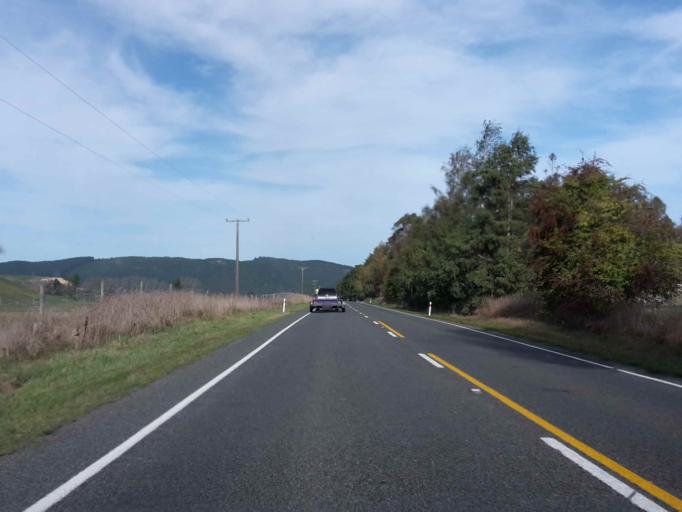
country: NZ
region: Canterbury
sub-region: Timaru District
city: Pleasant Point
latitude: -44.1105
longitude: 171.0123
